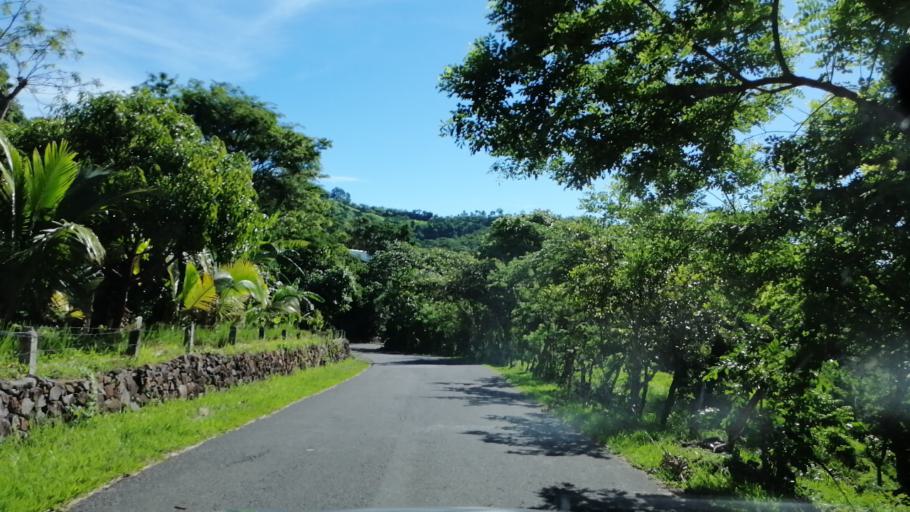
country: SV
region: Morazan
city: Corinto
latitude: 13.8112
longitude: -87.9869
